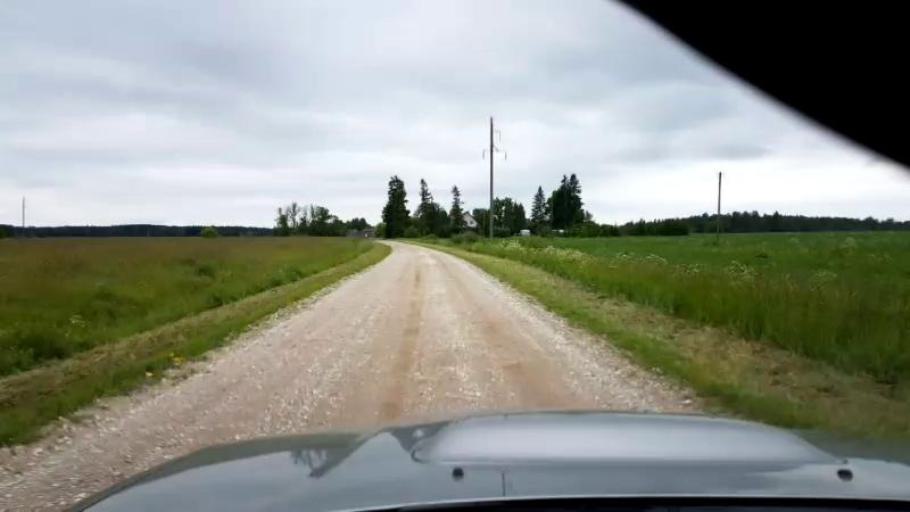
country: EE
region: Paernumaa
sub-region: Halinga vald
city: Parnu-Jaagupi
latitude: 58.5409
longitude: 24.5587
